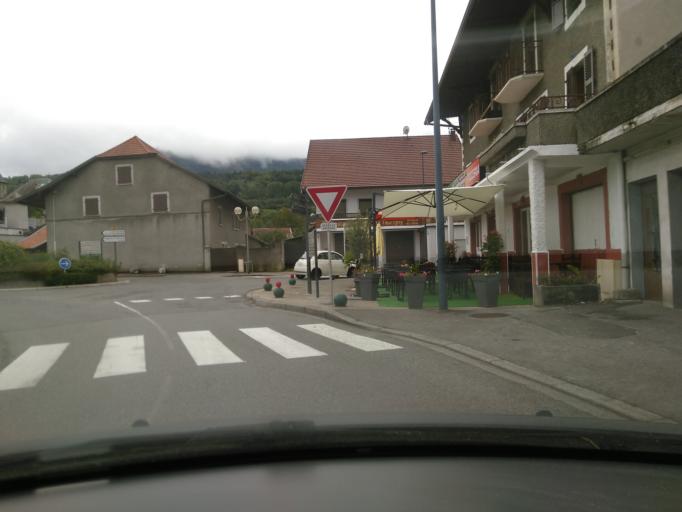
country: FR
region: Rhone-Alpes
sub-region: Departement de la Haute-Savoie
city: Amancy
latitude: 46.0599
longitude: 6.3635
